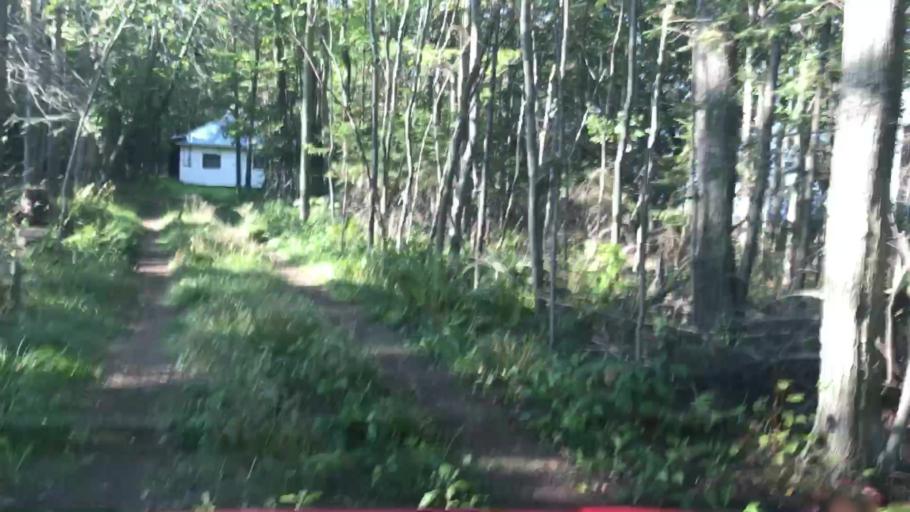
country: US
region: Michigan
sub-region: Chippewa County
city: Sault Ste. Marie
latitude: 46.2945
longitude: -84.0716
